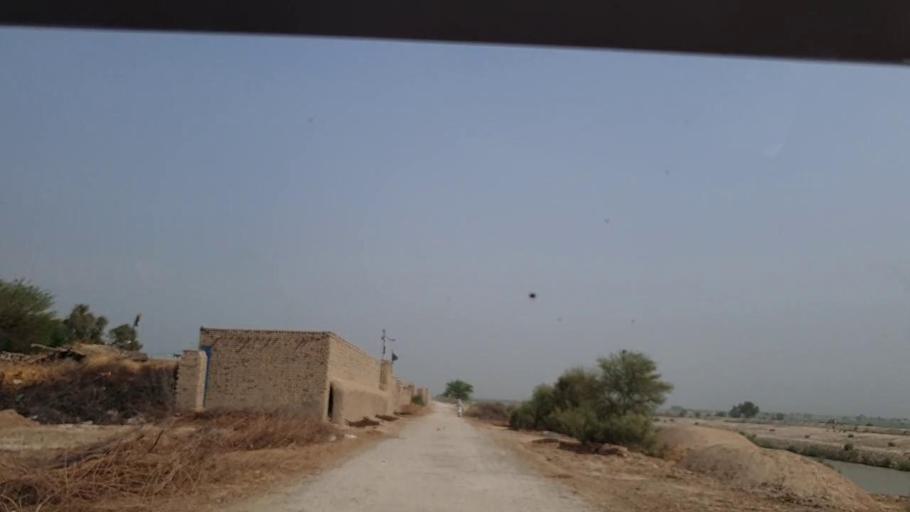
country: PK
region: Sindh
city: Khairpur Nathan Shah
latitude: 27.0241
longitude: 67.6736
